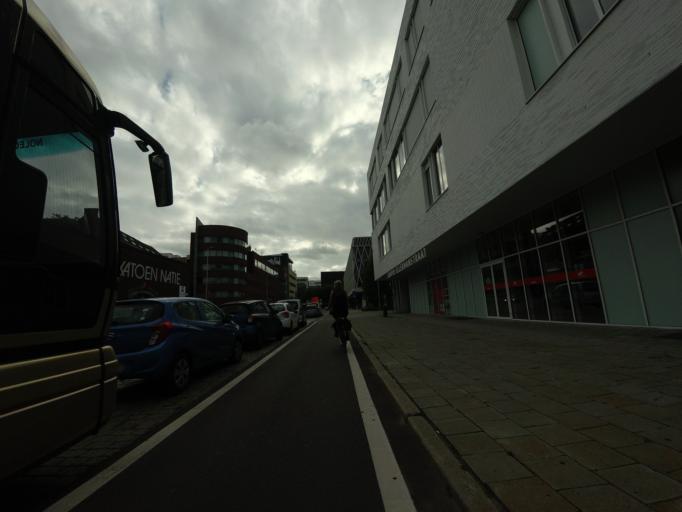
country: BE
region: Flanders
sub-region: Provincie Antwerpen
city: Antwerpen
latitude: 51.2299
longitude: 4.4161
